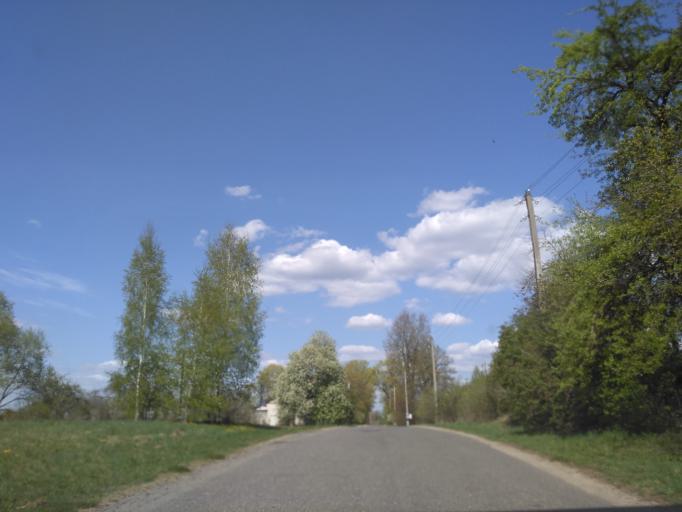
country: BY
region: Minsk
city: Narach
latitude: 54.9701
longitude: 26.6371
